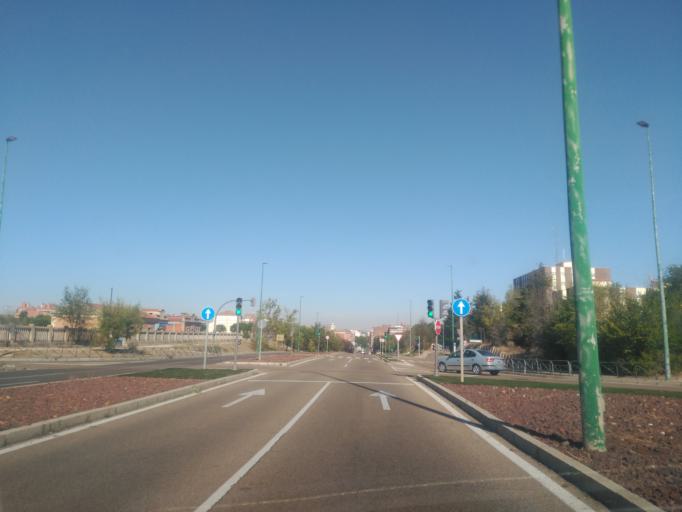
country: ES
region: Castille and Leon
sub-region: Provincia de Valladolid
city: Valladolid
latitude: 41.6393
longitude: -4.7097
